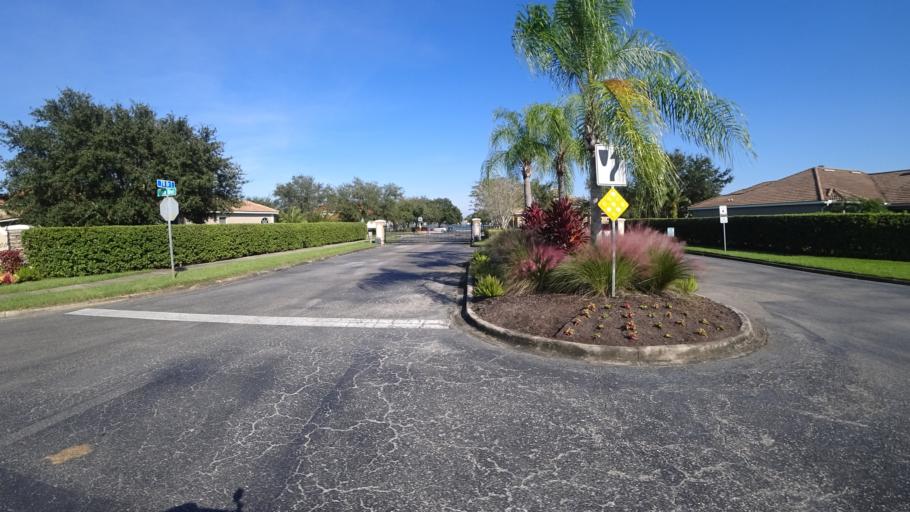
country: US
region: Florida
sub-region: Sarasota County
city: Desoto Lakes
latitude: 27.4154
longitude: -82.4636
